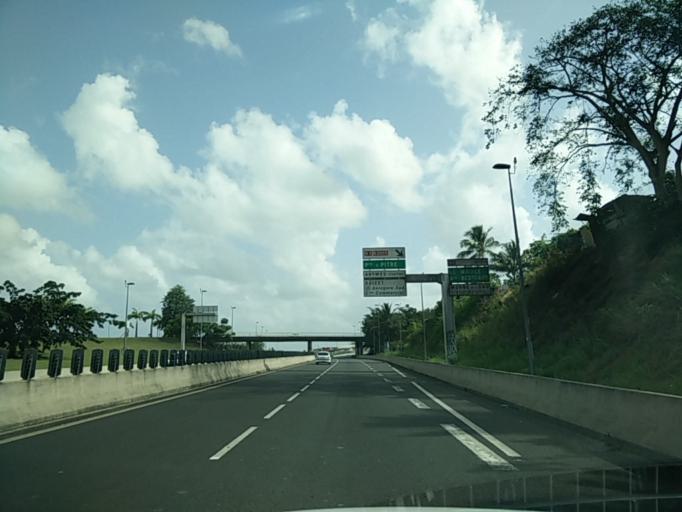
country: GP
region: Guadeloupe
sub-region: Guadeloupe
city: Les Abymes
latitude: 16.2635
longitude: -61.5111
